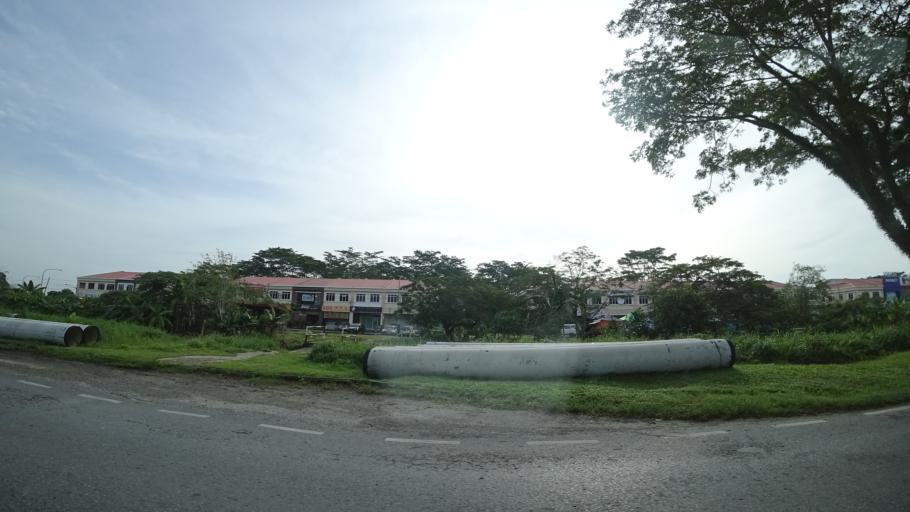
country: MY
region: Sarawak
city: Miri
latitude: 4.4763
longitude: 114.0420
